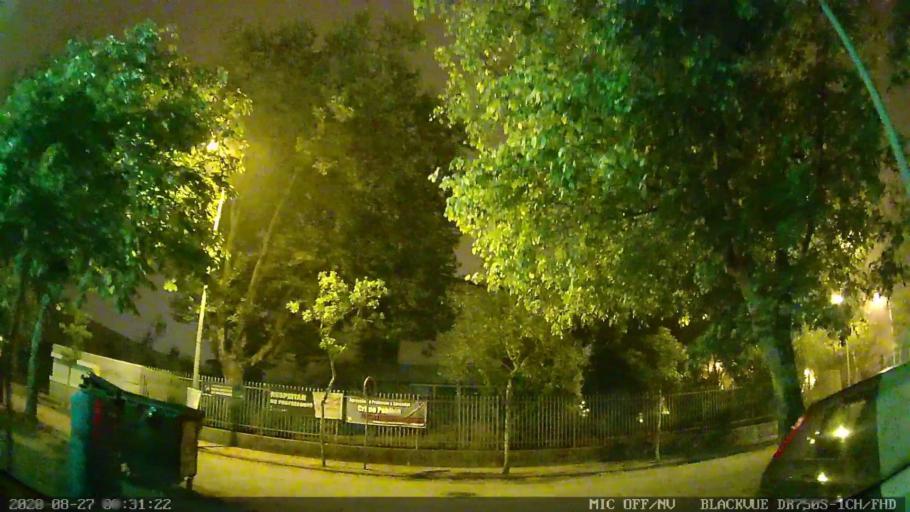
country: PT
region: Aveiro
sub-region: Aveiro
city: Aveiro
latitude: 40.6363
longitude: -8.6465
